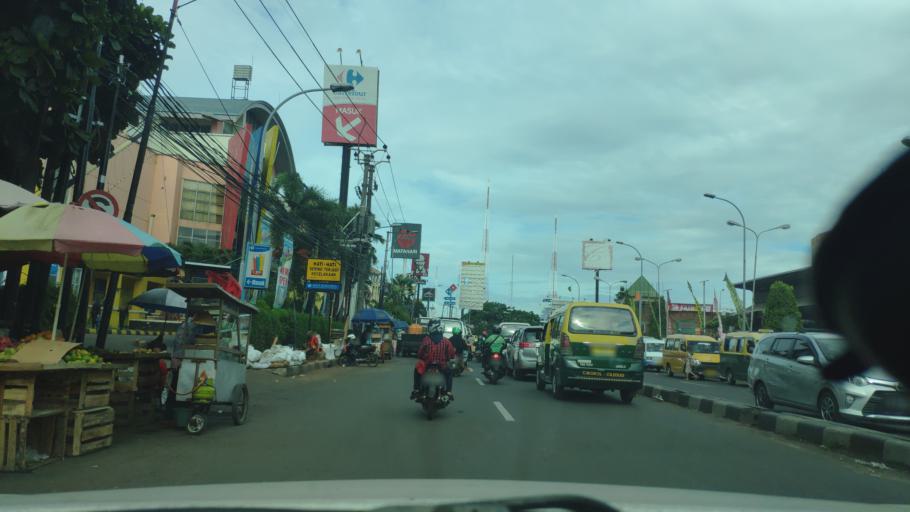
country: ID
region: West Java
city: Ciputat
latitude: -6.2250
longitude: 106.7076
